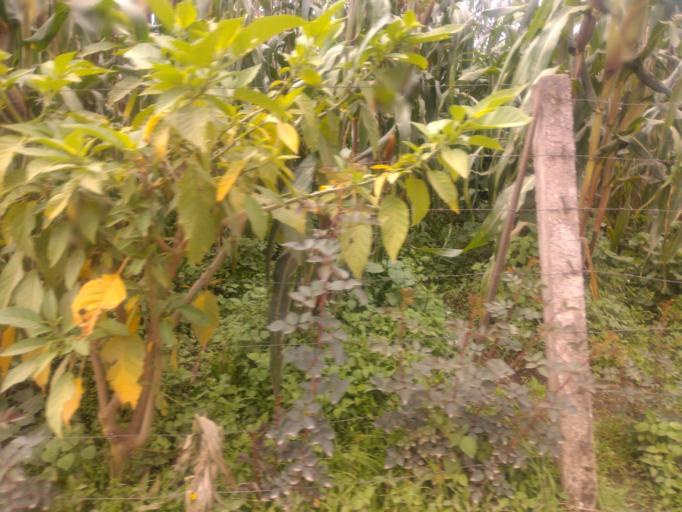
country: GT
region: Quetzaltenango
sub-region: Municipio de La Esperanza
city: La Esperanza
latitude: 14.8633
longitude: -91.5706
